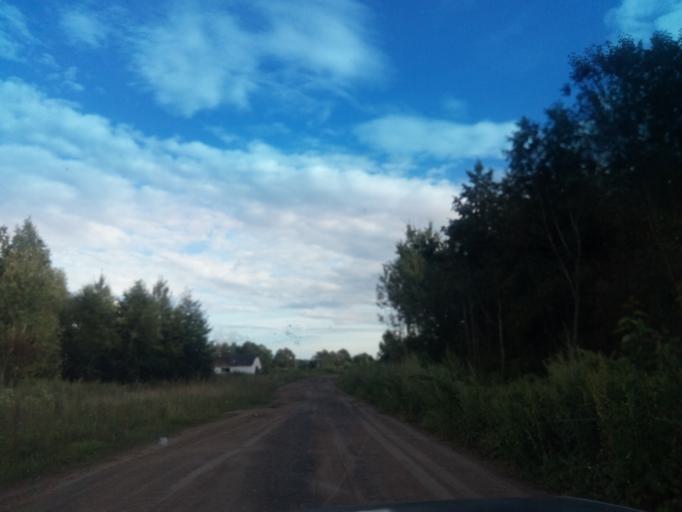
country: BY
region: Vitebsk
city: Dzisna
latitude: 55.6753
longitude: 28.3488
